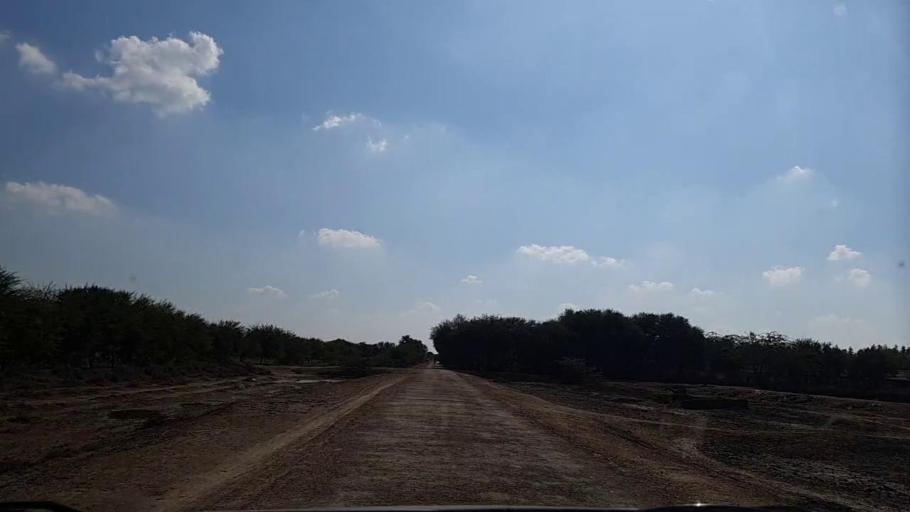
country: PK
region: Sindh
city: Pithoro
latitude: 25.6539
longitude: 69.4486
